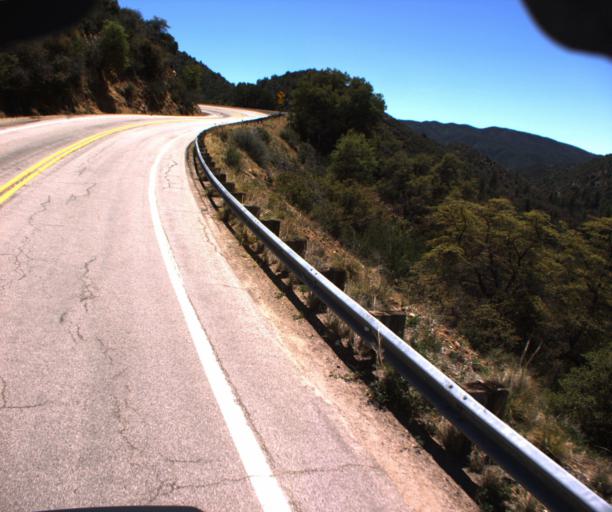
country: US
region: Arizona
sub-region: Yavapai County
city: Prescott
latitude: 34.4535
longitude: -112.5359
